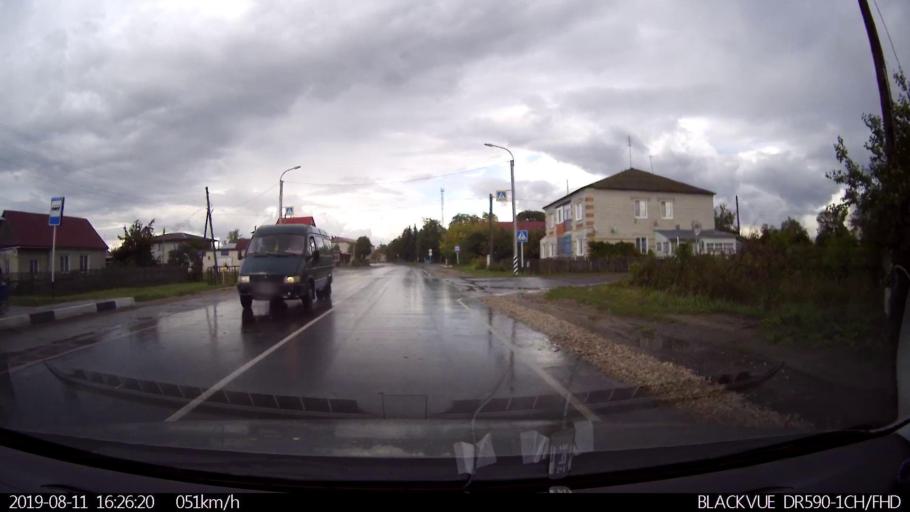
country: RU
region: Ulyanovsk
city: Mayna
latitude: 54.1099
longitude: 47.6153
